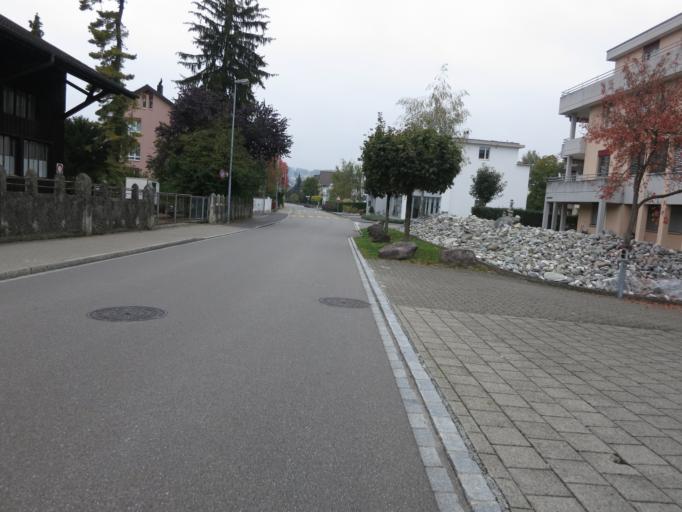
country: CH
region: Saint Gallen
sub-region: Wahlkreis See-Gaster
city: Rapperswil
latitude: 47.2298
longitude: 8.8243
